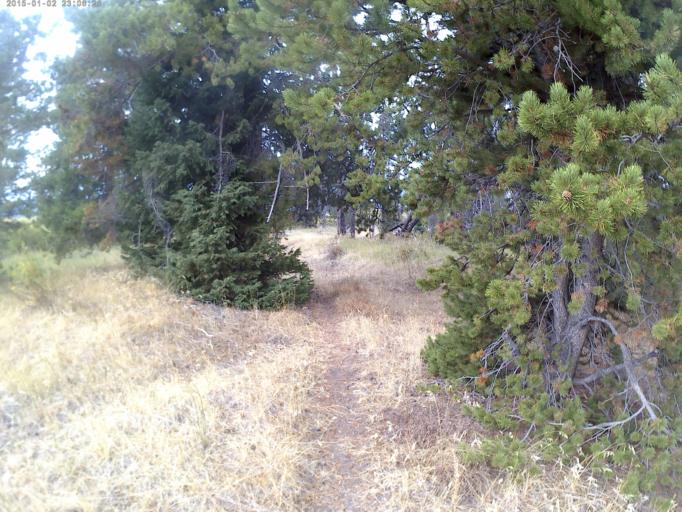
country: US
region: Wyoming
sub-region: Teton County
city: Moose Wilson Road
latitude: 43.8878
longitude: -110.6148
